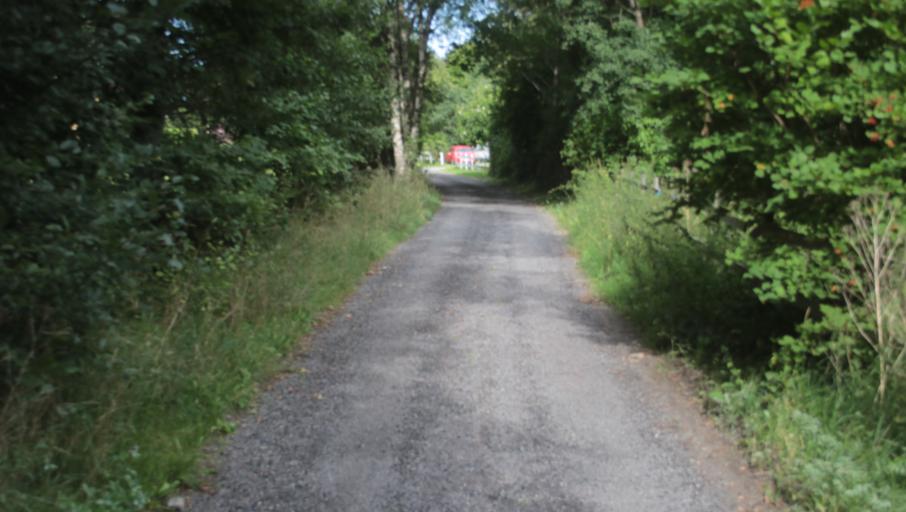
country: SE
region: Blekinge
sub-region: Karlshamns Kommun
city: Karlshamn
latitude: 56.2224
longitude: 14.8366
